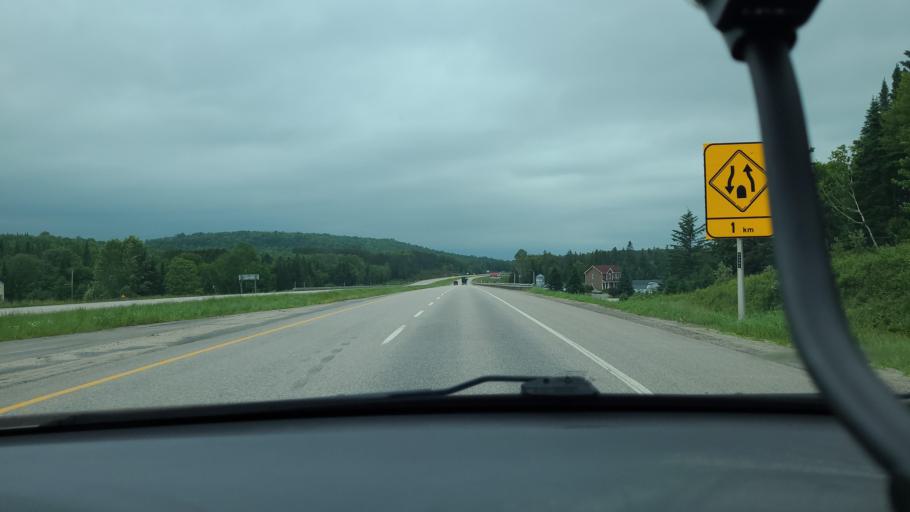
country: CA
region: Quebec
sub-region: Laurentides
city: Labelle
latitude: 46.2830
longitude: -74.7588
